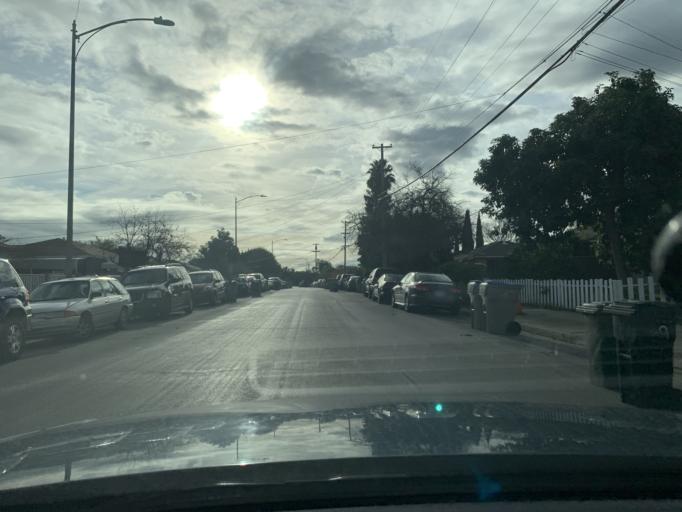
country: US
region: California
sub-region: Santa Clara County
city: Alum Rock
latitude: 37.3514
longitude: -121.8477
